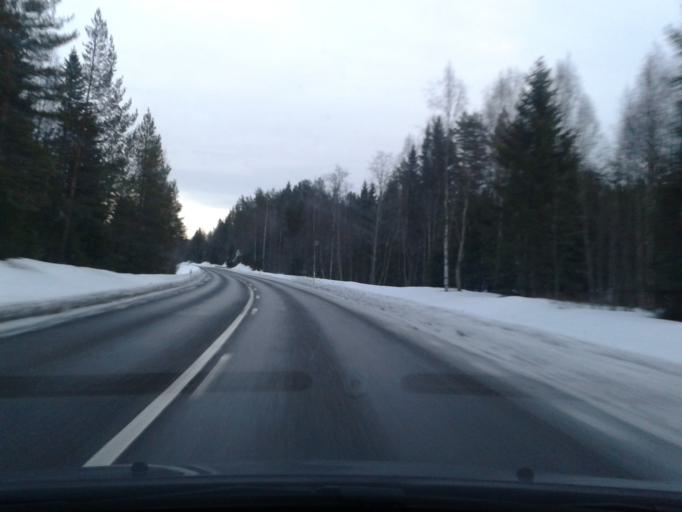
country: SE
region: Vaesternorrland
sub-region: Kramfors Kommun
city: Bollstabruk
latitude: 63.1010
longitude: 17.5132
